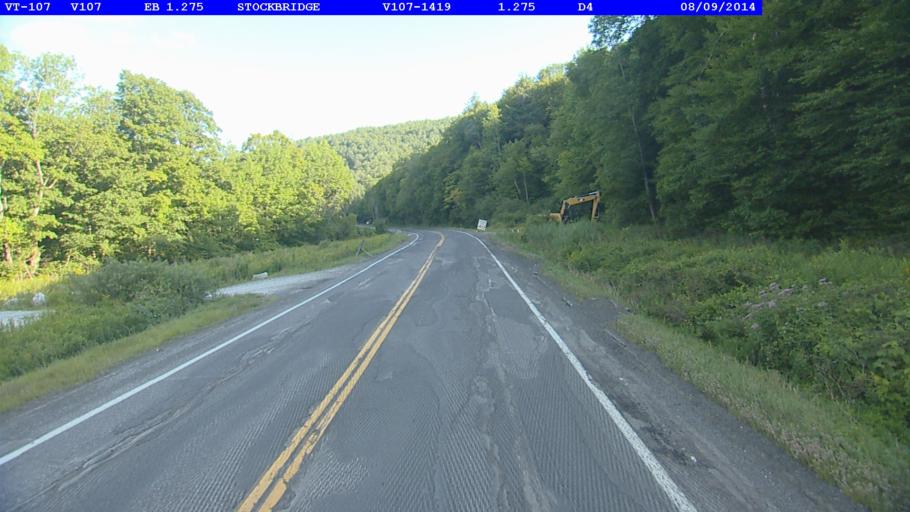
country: US
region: Vermont
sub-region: Orange County
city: Randolph
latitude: 43.7645
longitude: -72.7434
